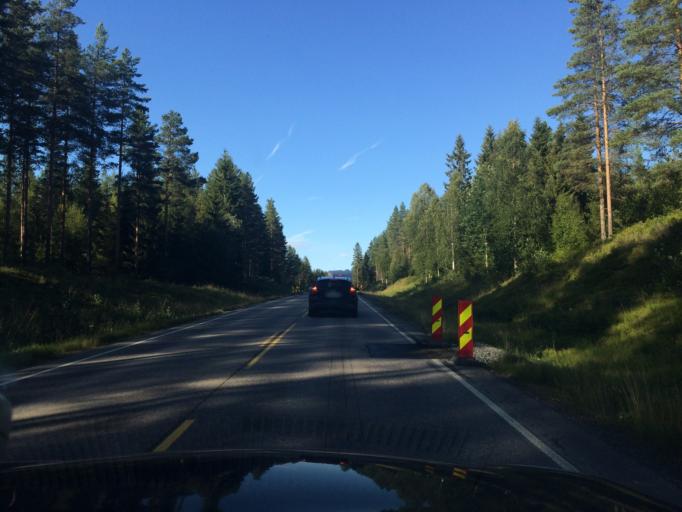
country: NO
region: Hedmark
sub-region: Elverum
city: Elverum
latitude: 60.9597
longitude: 11.7090
